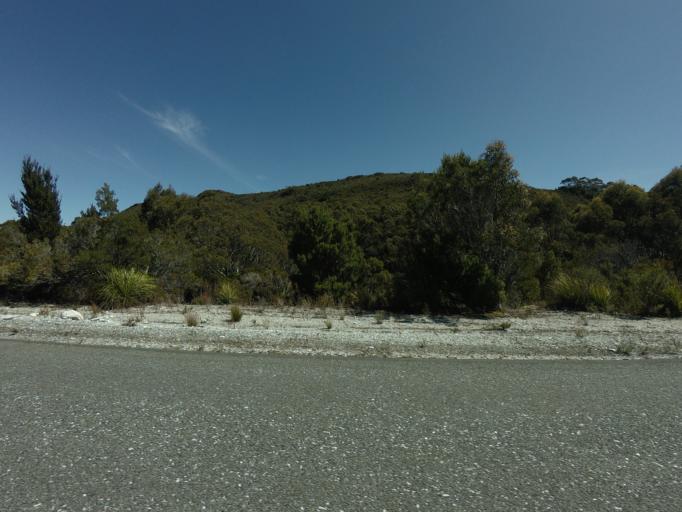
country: AU
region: Tasmania
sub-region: West Coast
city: Queenstown
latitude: -42.7928
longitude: 146.0644
